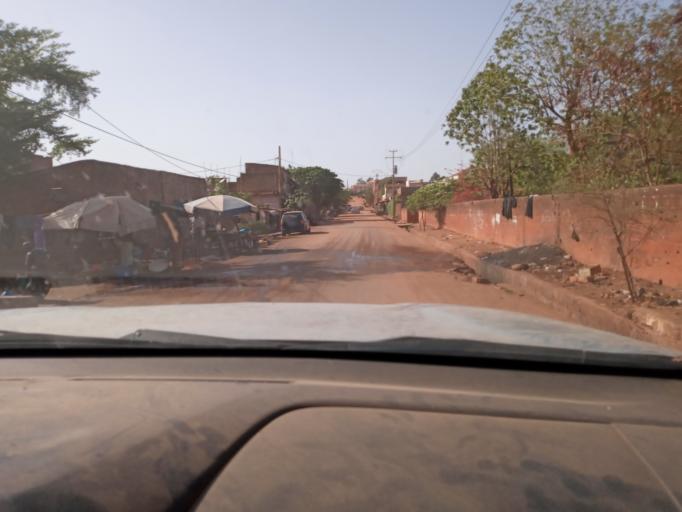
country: ML
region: Bamako
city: Bamako
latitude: 12.6705
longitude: -7.9178
